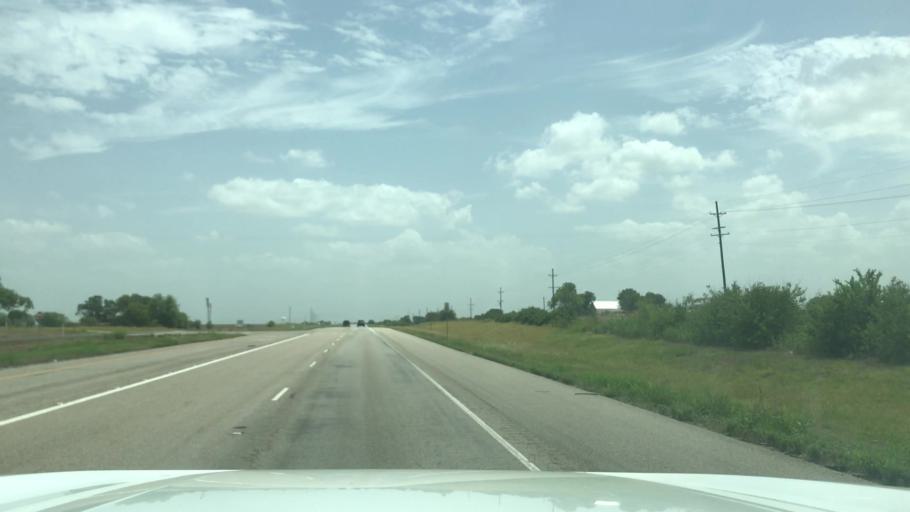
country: US
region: Texas
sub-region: Falls County
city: Marlin
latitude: 31.3476
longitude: -96.8950
